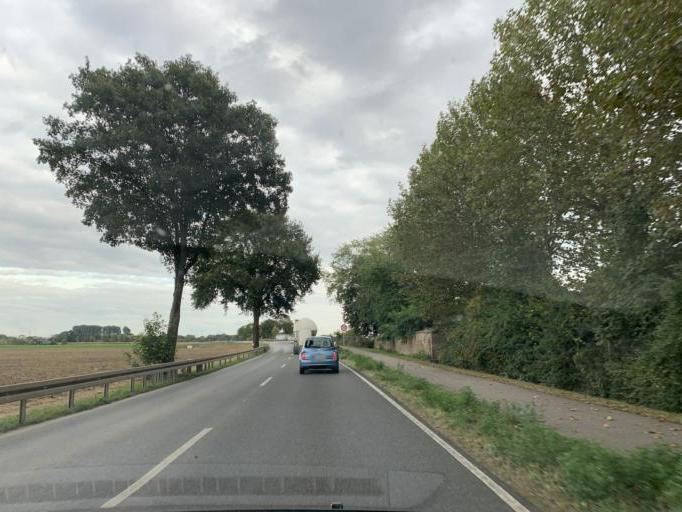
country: DE
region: North Rhine-Westphalia
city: Huckelhoven
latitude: 51.0458
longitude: 6.1984
